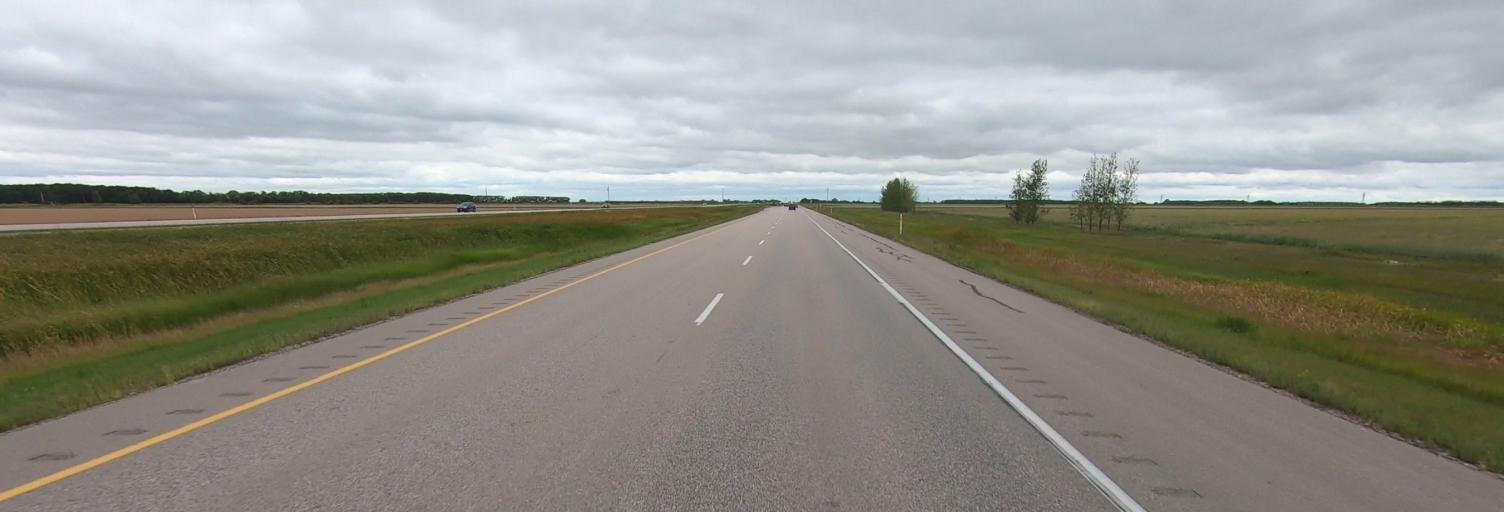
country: CA
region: Manitoba
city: Headingley
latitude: 49.9231
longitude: -97.8437
